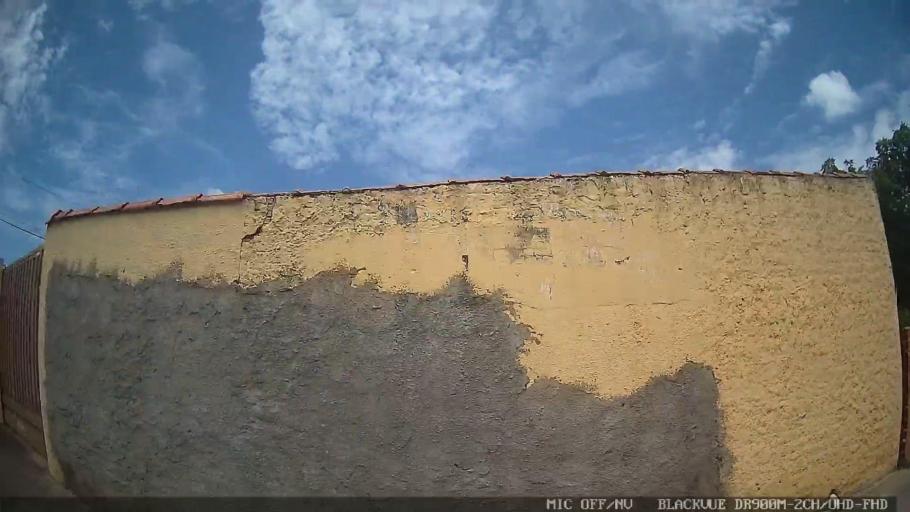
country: BR
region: Sao Paulo
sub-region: Laranjal Paulista
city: Laranjal Paulista
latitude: -23.0390
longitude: -47.8269
